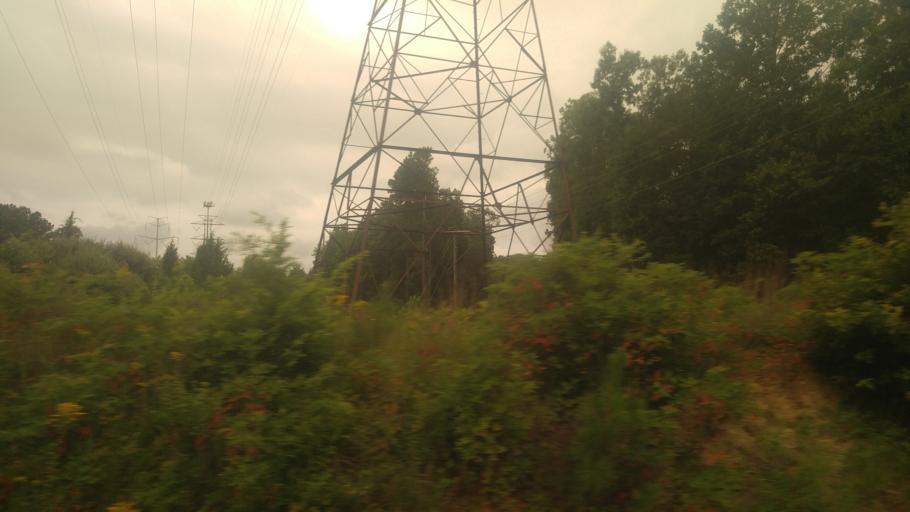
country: US
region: Virginia
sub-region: Henrico County
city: Glen Allen
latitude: 37.6777
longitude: -77.5032
